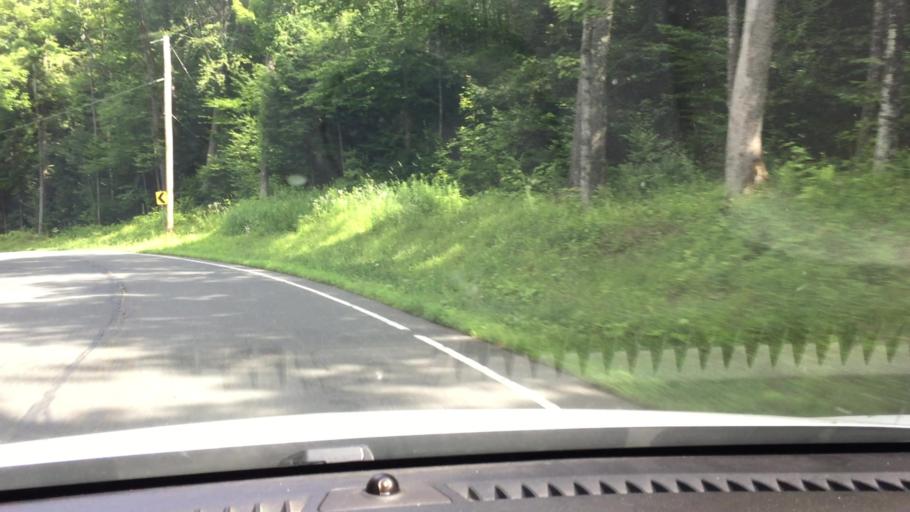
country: US
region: Massachusetts
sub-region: Berkshire County
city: Otis
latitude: 42.2101
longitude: -73.1723
